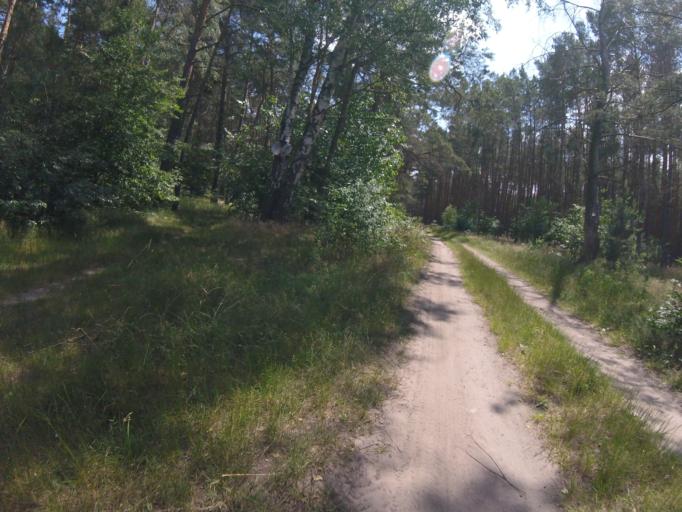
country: DE
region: Brandenburg
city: Bestensee
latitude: 52.2740
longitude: 13.6877
